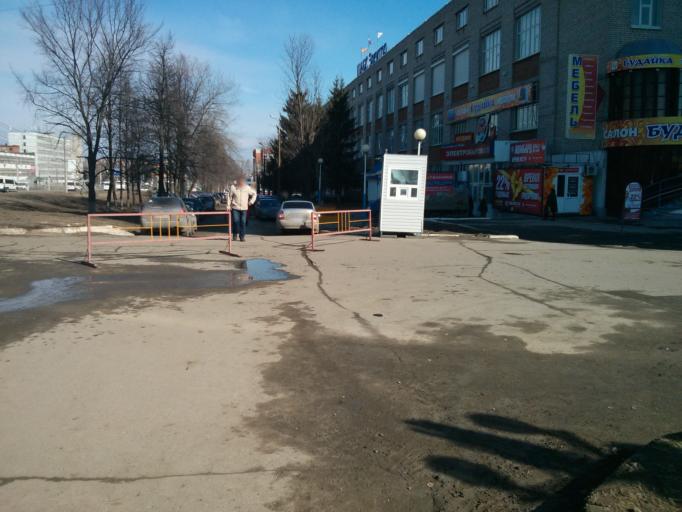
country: RU
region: Chuvashia
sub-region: Cheboksarskiy Rayon
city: Cheboksary
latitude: 56.1023
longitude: 47.2638
